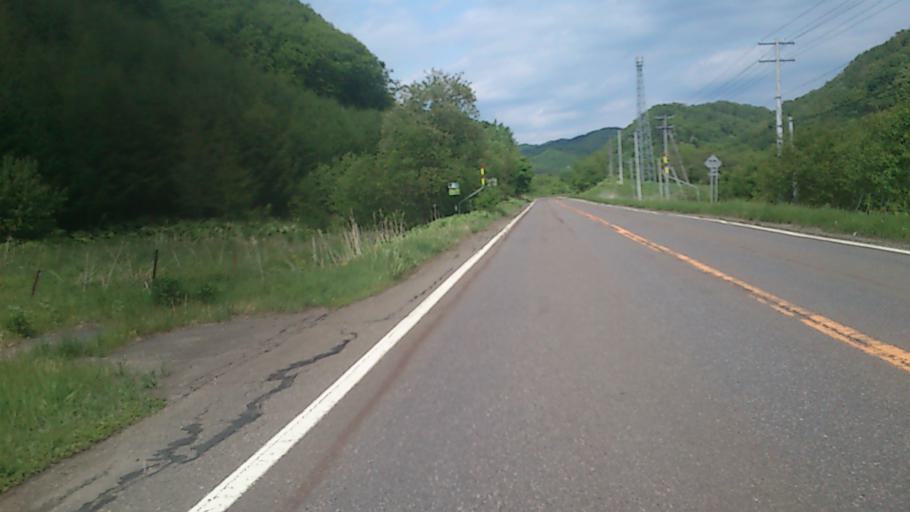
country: JP
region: Hokkaido
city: Kitami
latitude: 43.3457
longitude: 143.7724
